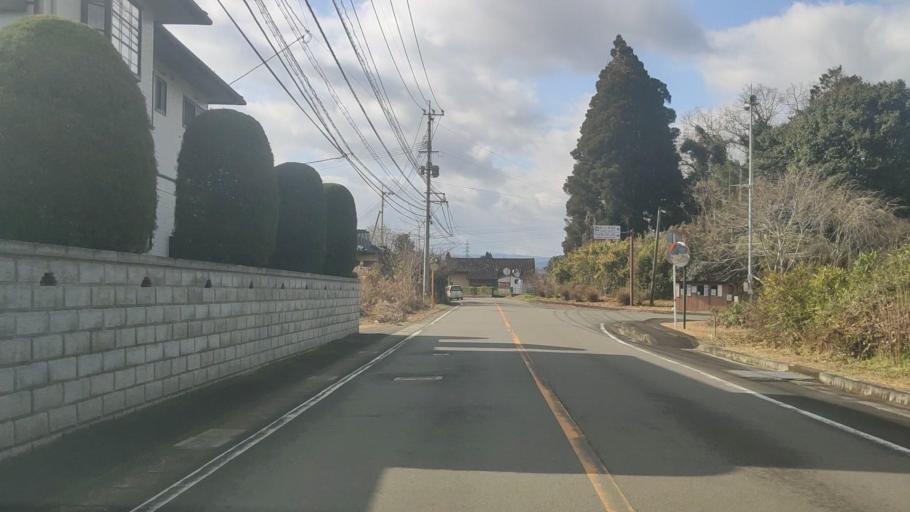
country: JP
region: Kumamoto
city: Hitoyoshi
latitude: 32.2287
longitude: 130.7830
